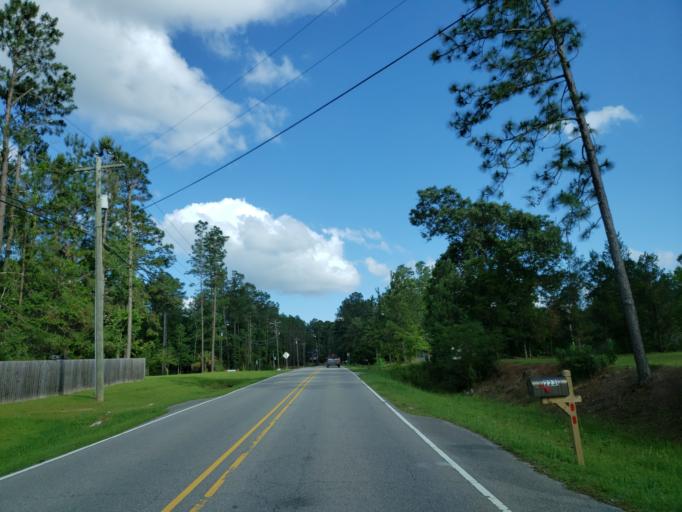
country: US
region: Mississippi
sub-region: Lamar County
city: West Hattiesburg
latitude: 31.2867
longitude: -89.4396
